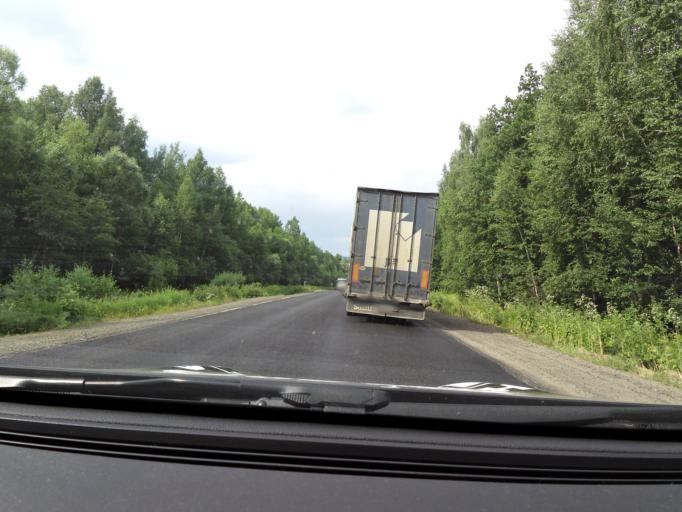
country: RU
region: Chelyabinsk
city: Asha
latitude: 54.8616
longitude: 57.1600
